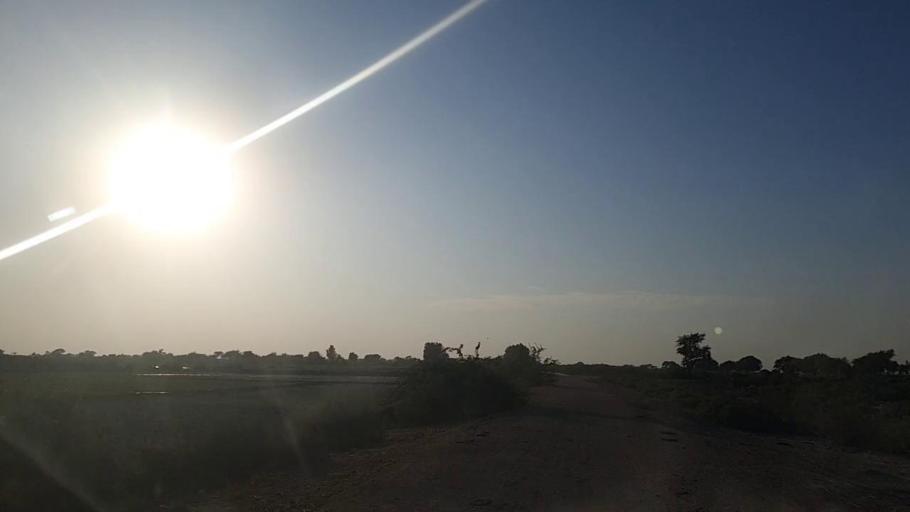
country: PK
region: Sindh
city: Jati
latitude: 24.4160
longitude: 68.1749
